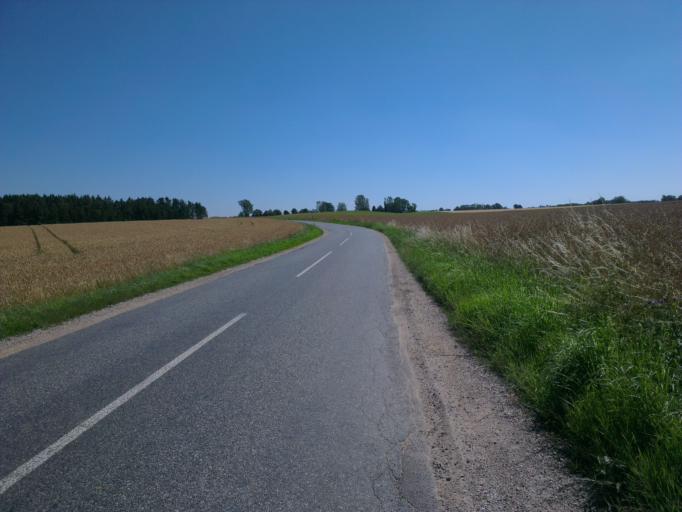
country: DK
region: Capital Region
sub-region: Egedal Kommune
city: Olstykke
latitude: 55.8351
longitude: 12.1244
